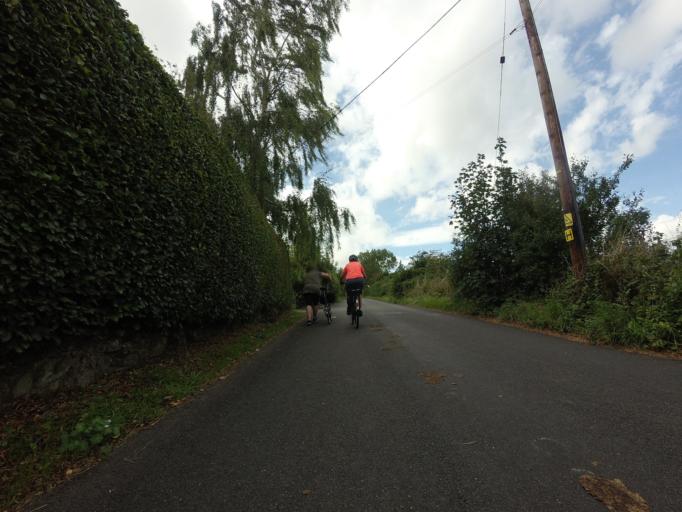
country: GB
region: England
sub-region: Kent
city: Shoreham
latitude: 51.3146
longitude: 0.1655
